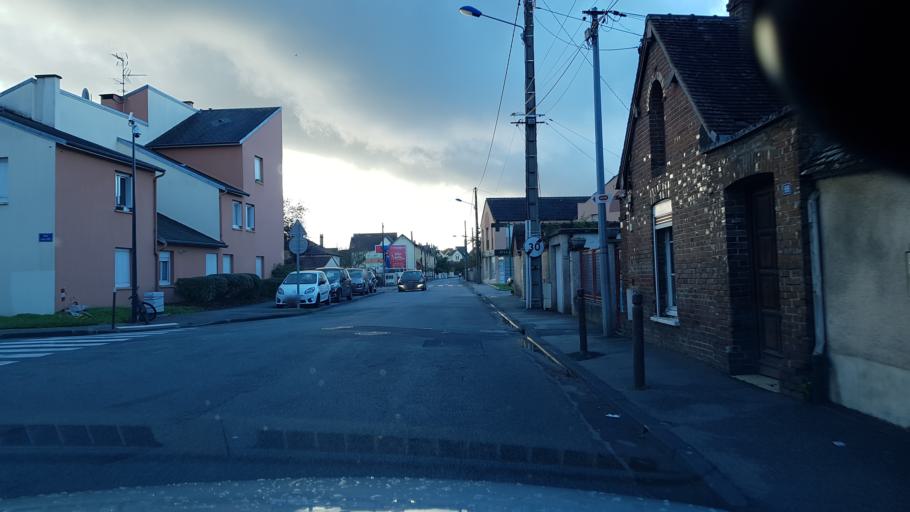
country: FR
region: Haute-Normandie
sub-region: Departement de l'Eure
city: Evreux
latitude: 49.0177
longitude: 1.1299
